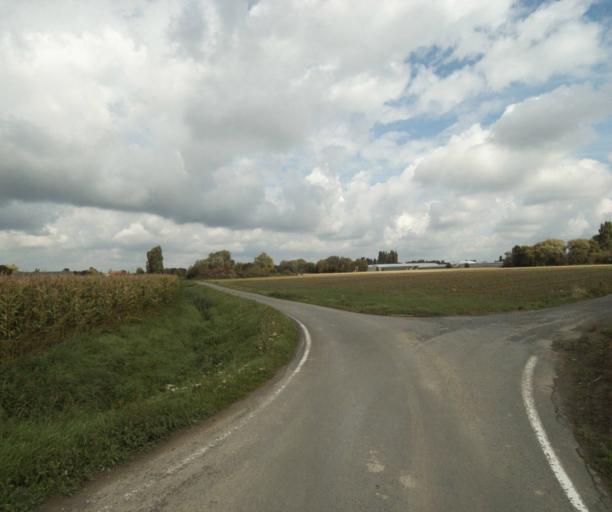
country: FR
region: Nord-Pas-de-Calais
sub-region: Departement du Nord
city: Perenchies
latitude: 50.6797
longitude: 2.9697
